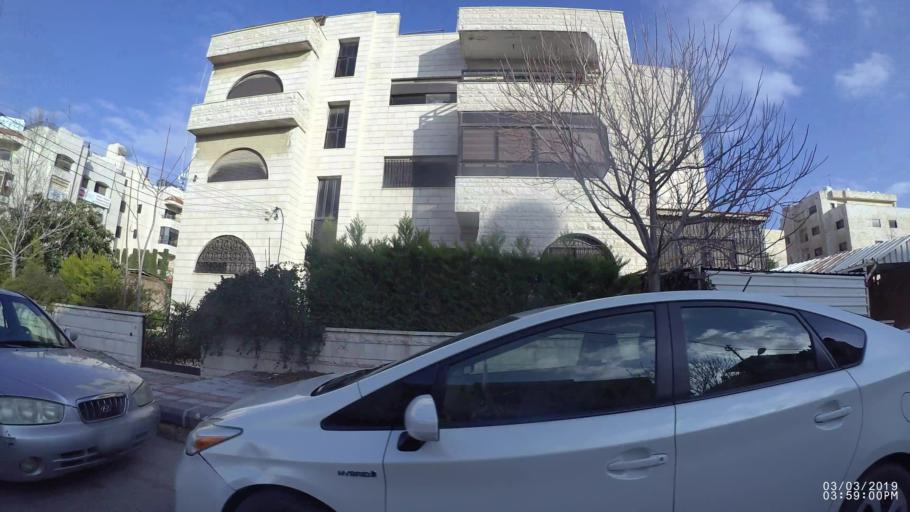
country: JO
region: Amman
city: Al Jubayhah
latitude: 31.9887
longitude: 35.8721
